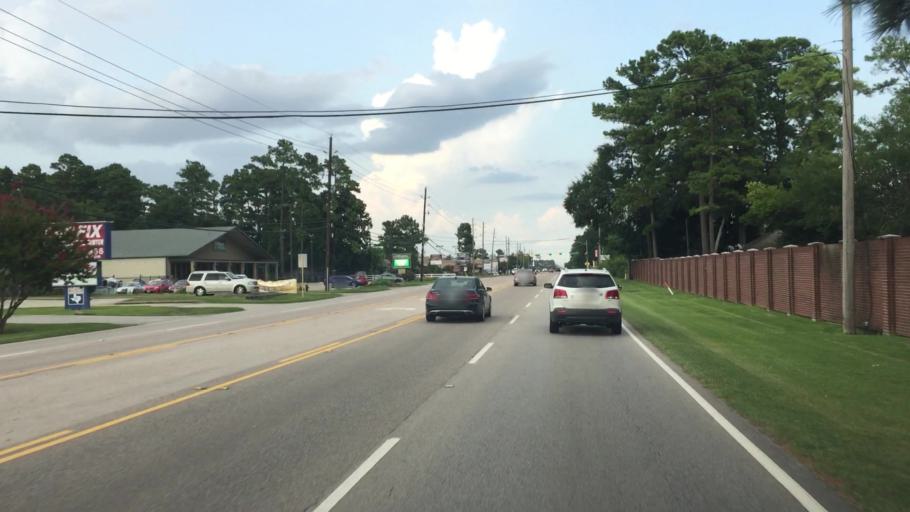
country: US
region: Texas
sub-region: Harris County
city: Spring
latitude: 30.0253
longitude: -95.5158
